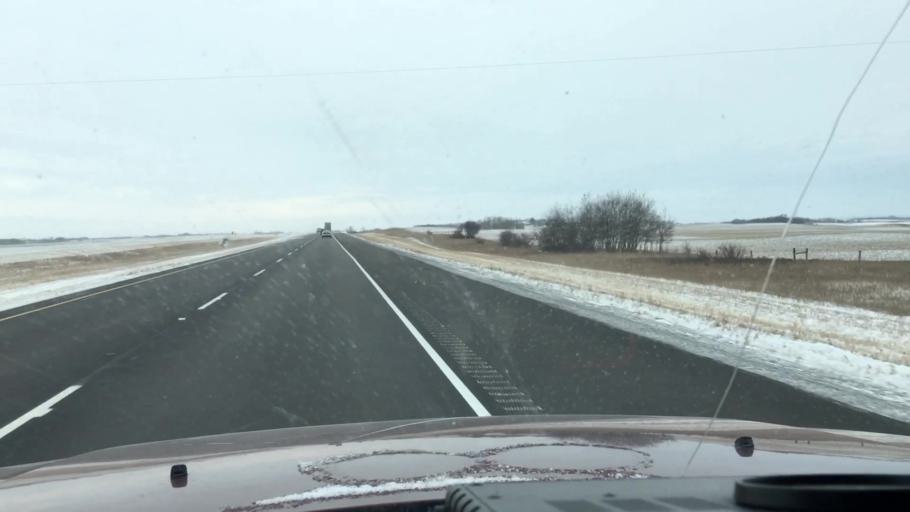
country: CA
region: Saskatchewan
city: Saskatoon
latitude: 51.7000
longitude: -106.4614
